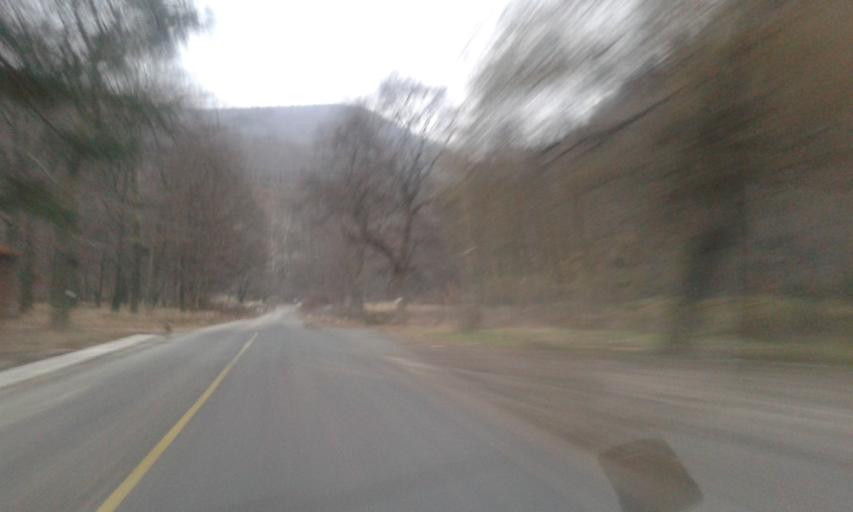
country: RO
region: Gorj
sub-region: Comuna Bumbesti-Jiu
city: Bumbesti-Jiu
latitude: 45.2593
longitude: 23.3877
